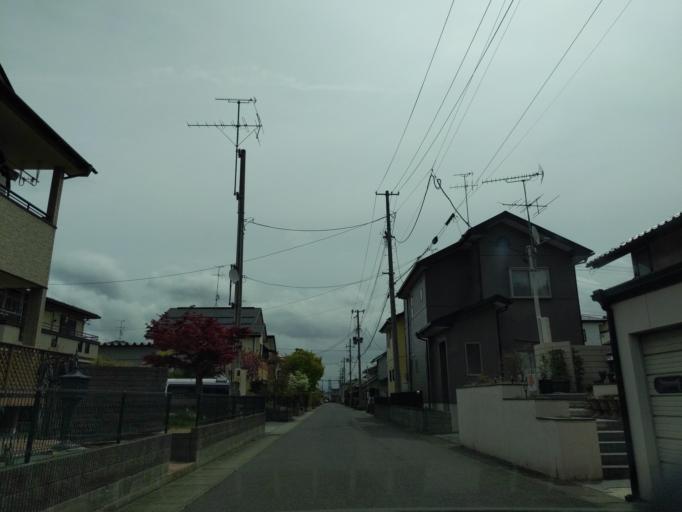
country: JP
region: Fukushima
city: Koriyama
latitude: 37.3888
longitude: 140.3265
